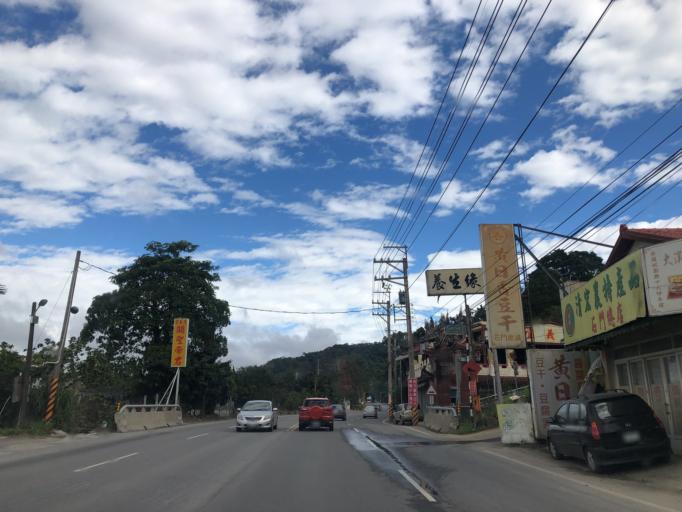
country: TW
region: Taiwan
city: Daxi
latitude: 24.8270
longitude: 121.2663
